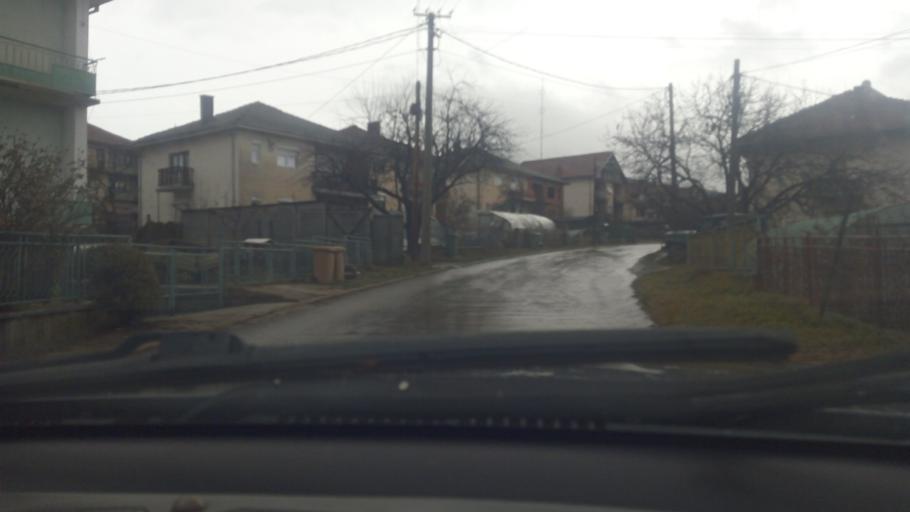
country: MK
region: Pehcevo
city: Pehcevo
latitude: 41.7646
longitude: 22.8849
